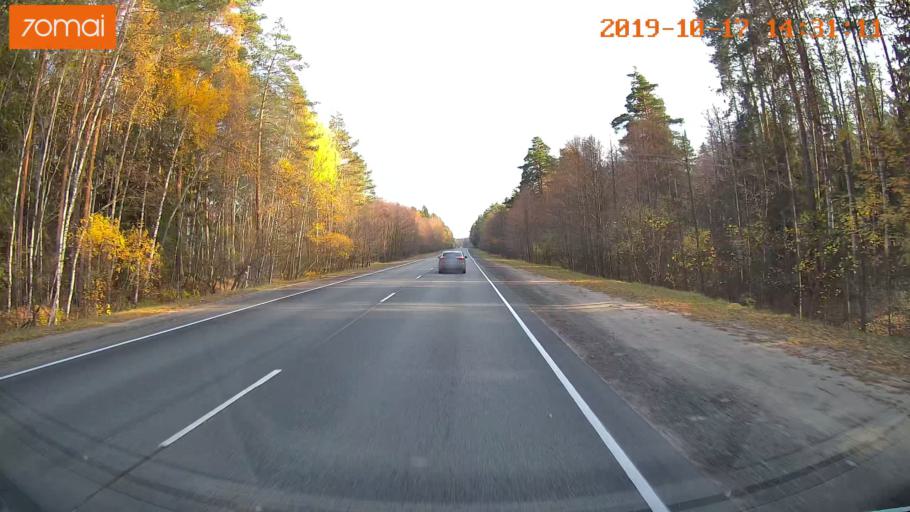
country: RU
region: Rjazan
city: Solotcha
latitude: 54.9390
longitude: 39.9572
